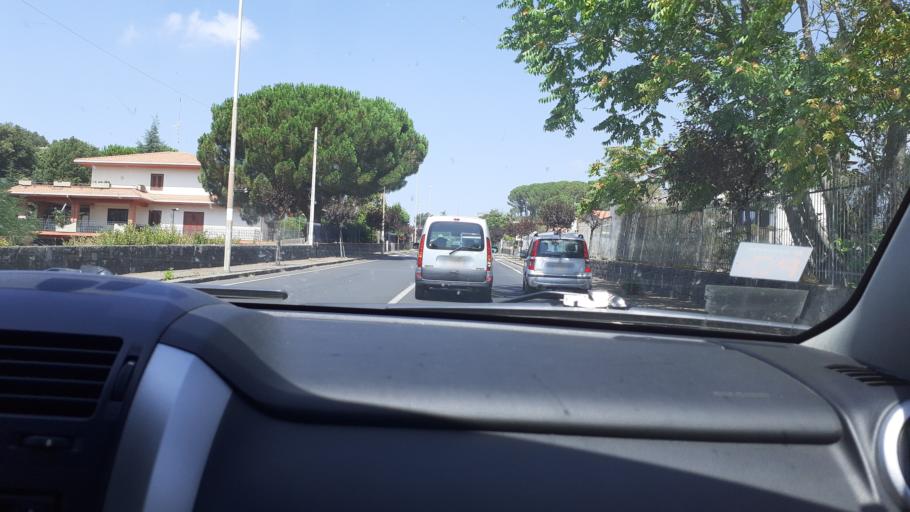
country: IT
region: Sicily
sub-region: Catania
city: Nicolosi
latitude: 37.6153
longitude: 15.0350
